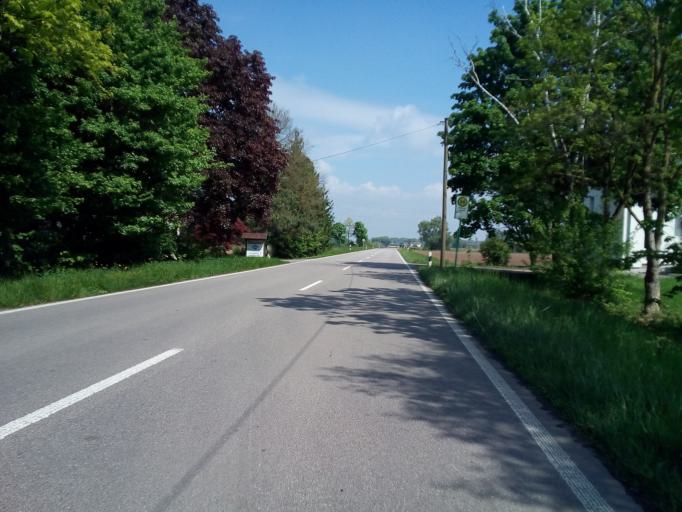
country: DE
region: Baden-Wuerttemberg
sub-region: Freiburg Region
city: Rheinau
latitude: 48.6611
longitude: 7.9932
